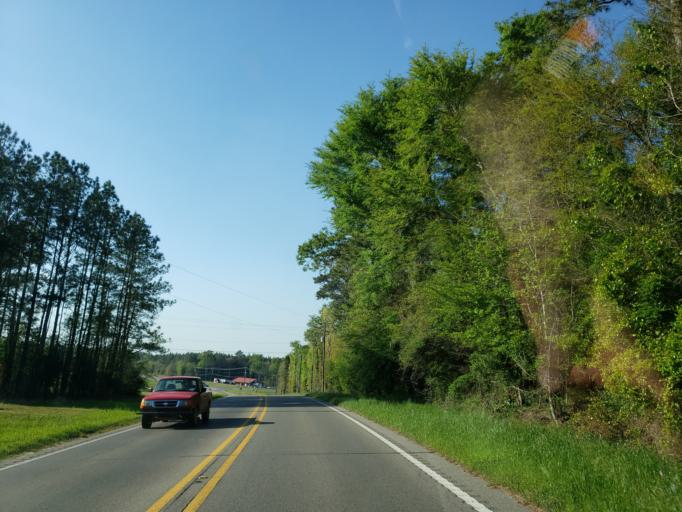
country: US
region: Mississippi
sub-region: Jones County
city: Laurel
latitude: 31.6756
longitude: -89.1093
